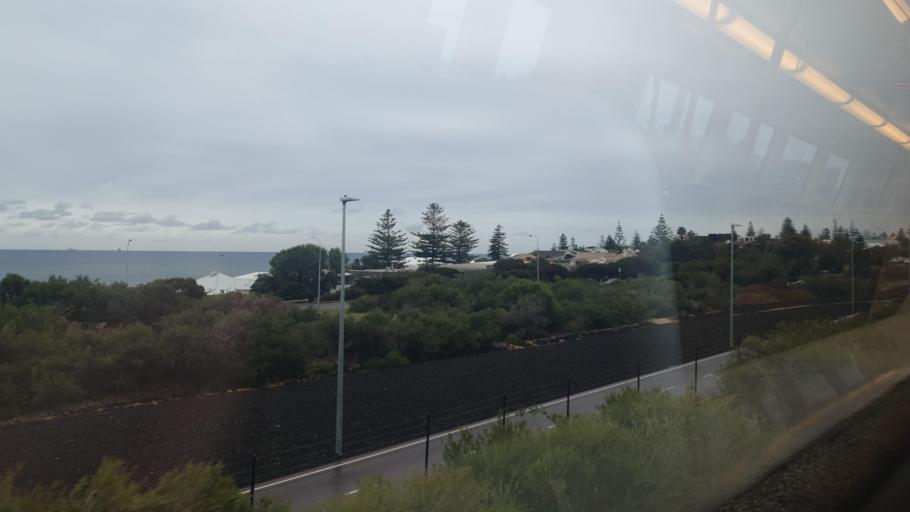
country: AU
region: Western Australia
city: Mosman Park
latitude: -32.0142
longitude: 115.7543
